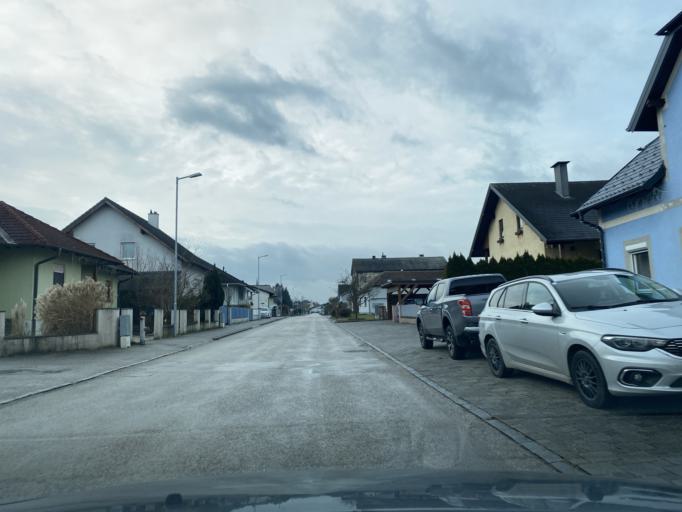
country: AT
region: Lower Austria
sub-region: Politischer Bezirk Sankt Polten
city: Prinzersdorf
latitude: 48.1965
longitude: 15.5066
